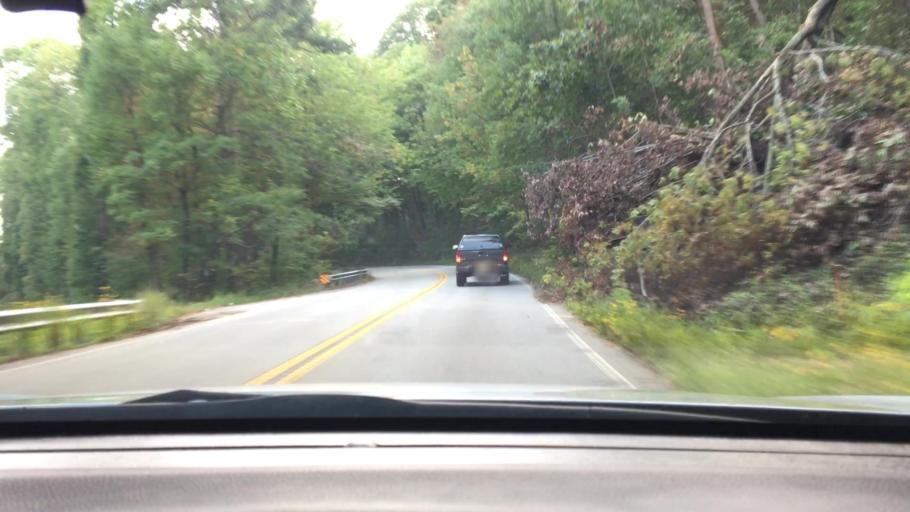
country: US
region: Tennessee
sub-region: Hamilton County
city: Lookout Mountain
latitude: 34.9996
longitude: -85.3344
